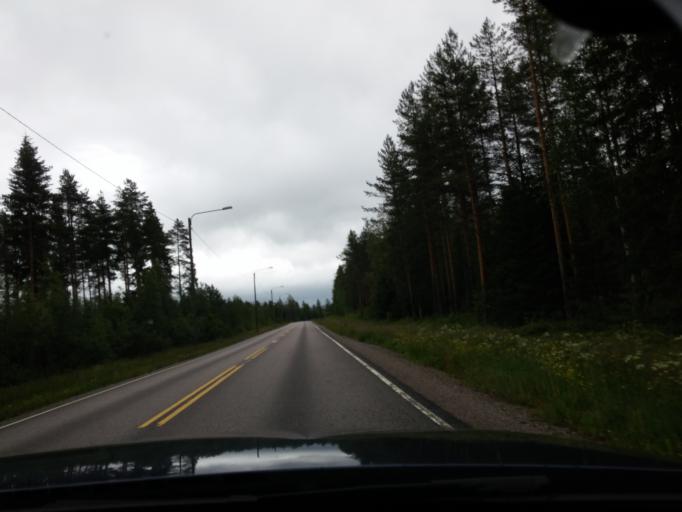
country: FI
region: Central Finland
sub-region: Saarijaervi-Viitasaari
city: Pylkoenmaeki
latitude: 62.6394
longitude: 24.8309
